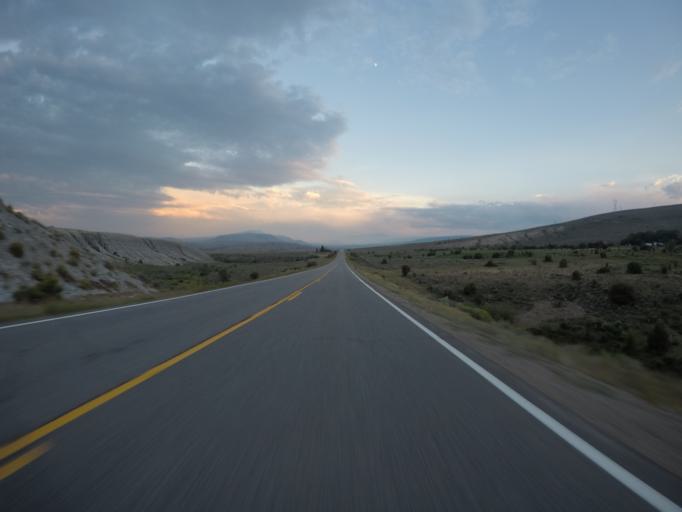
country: US
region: Colorado
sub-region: Grand County
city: Kremmling
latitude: 40.1092
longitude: -106.4261
